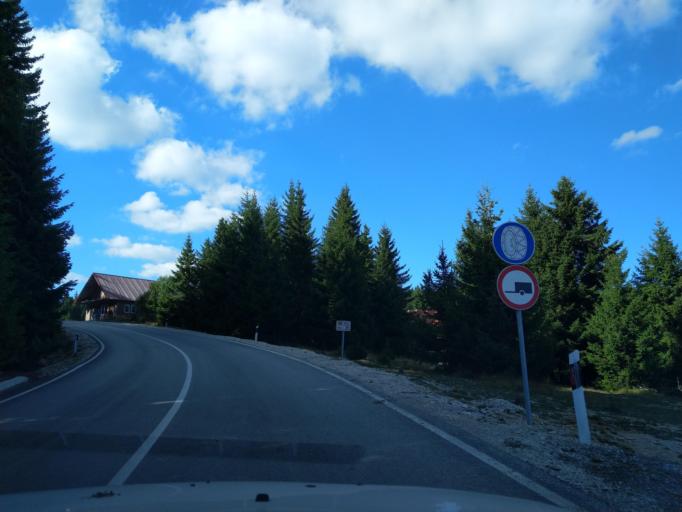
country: RS
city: Sokolovica
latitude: 43.2798
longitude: 20.3370
